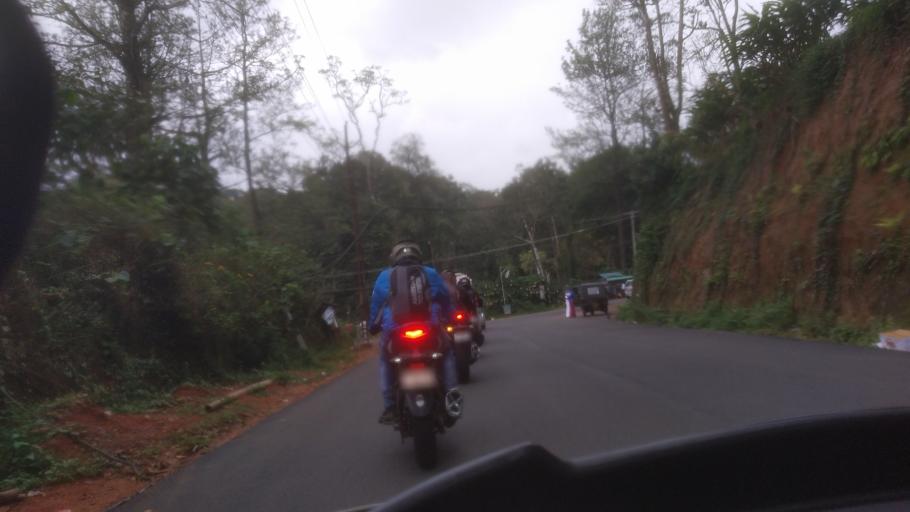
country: IN
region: Tamil Nadu
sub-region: Theni
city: Kombai
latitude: 9.8910
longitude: 77.1557
